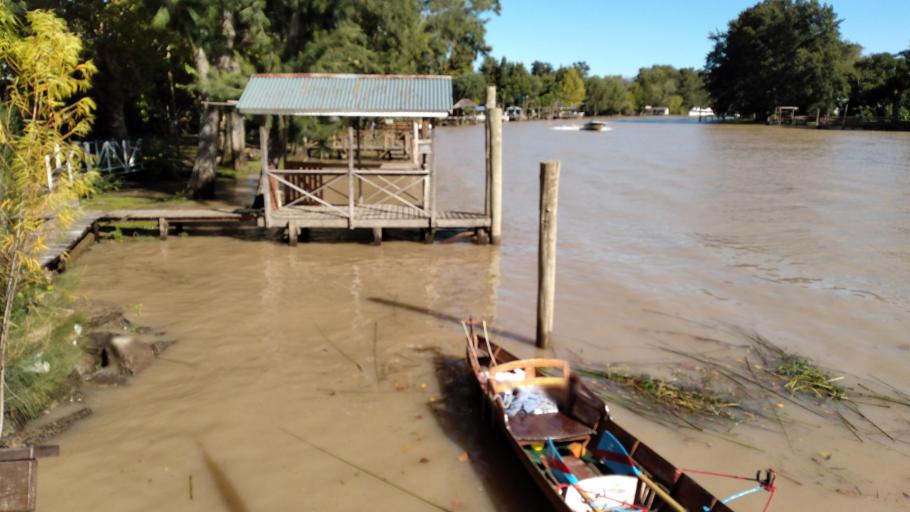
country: AR
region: Buenos Aires
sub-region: Partido de Tigre
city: Tigre
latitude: -34.3830
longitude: -58.5598
